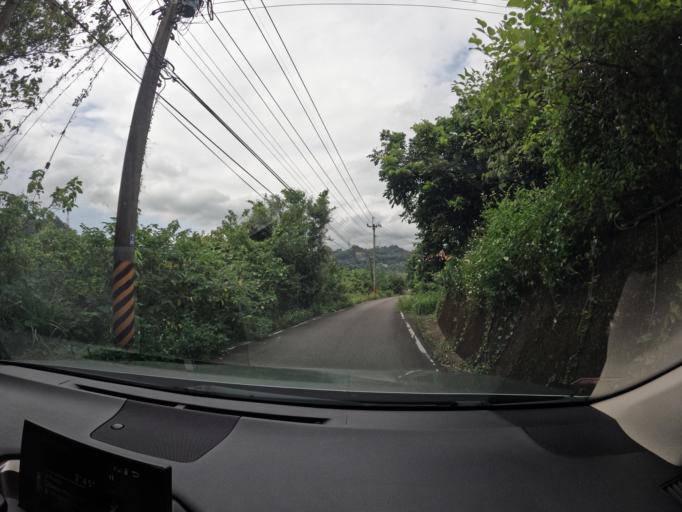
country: TW
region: Taiwan
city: Fengyuan
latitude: 24.3472
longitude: 120.8733
